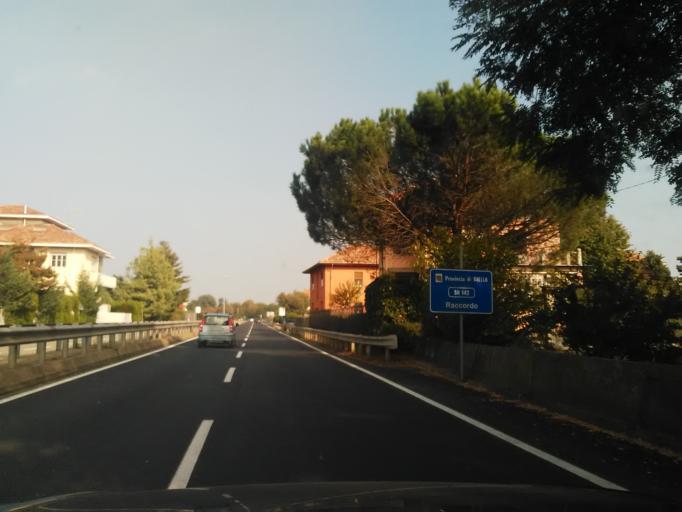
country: IT
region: Piedmont
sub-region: Provincia di Biella
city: Ponderano
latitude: 45.5493
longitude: 8.0675
